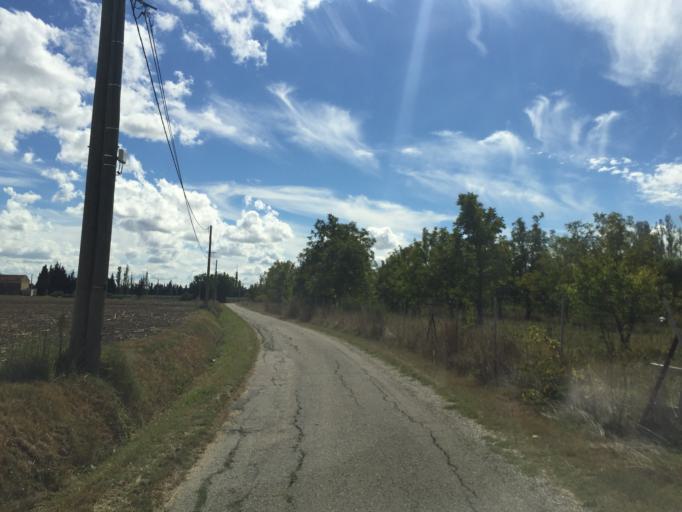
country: FR
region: Provence-Alpes-Cote d'Azur
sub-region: Departement du Vaucluse
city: Caderousse
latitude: 44.1171
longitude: 4.7366
